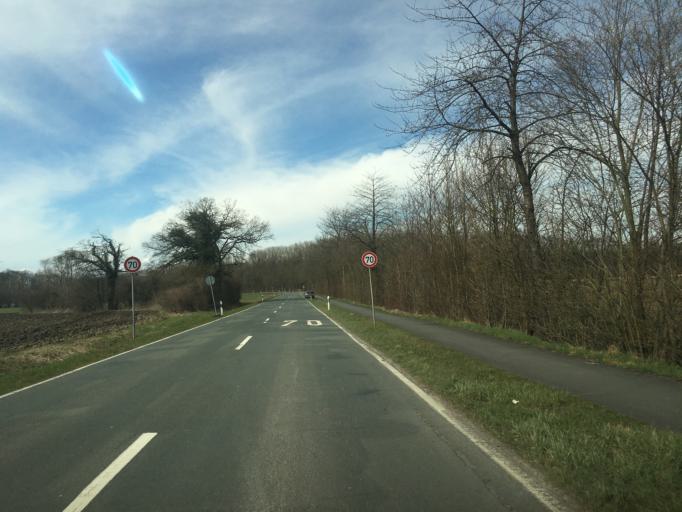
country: DE
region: North Rhine-Westphalia
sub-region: Regierungsbezirk Munster
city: Nordkirchen
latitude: 51.7296
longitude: 7.5648
